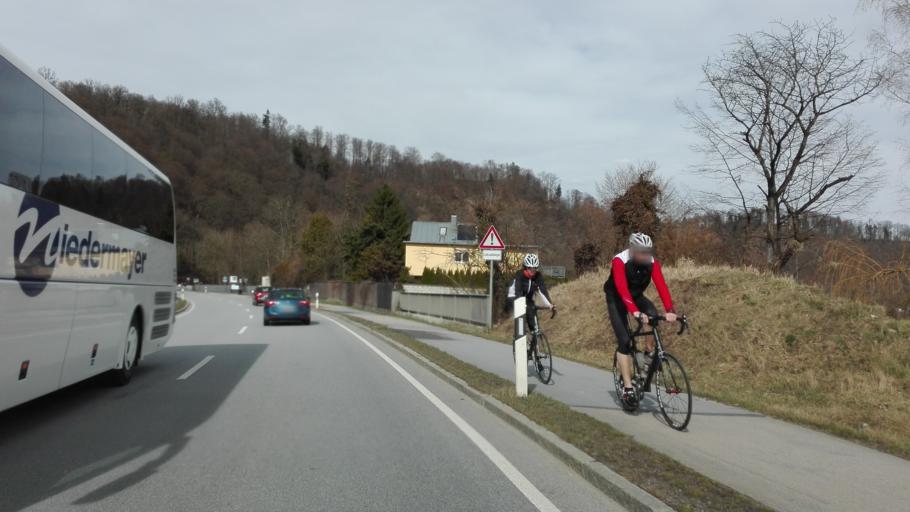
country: DE
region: Bavaria
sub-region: Lower Bavaria
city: Salzweg
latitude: 48.5882
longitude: 13.5040
